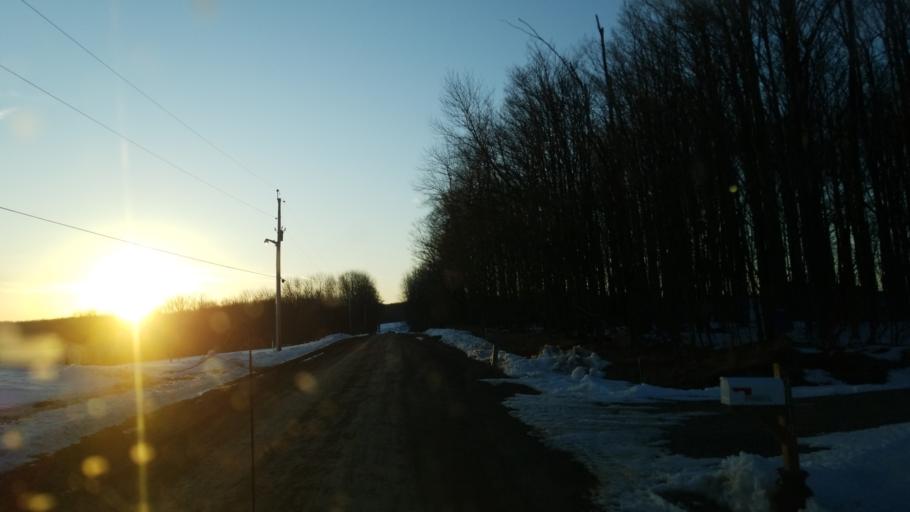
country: US
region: Pennsylvania
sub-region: Tioga County
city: Westfield
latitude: 42.0394
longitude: -77.6145
